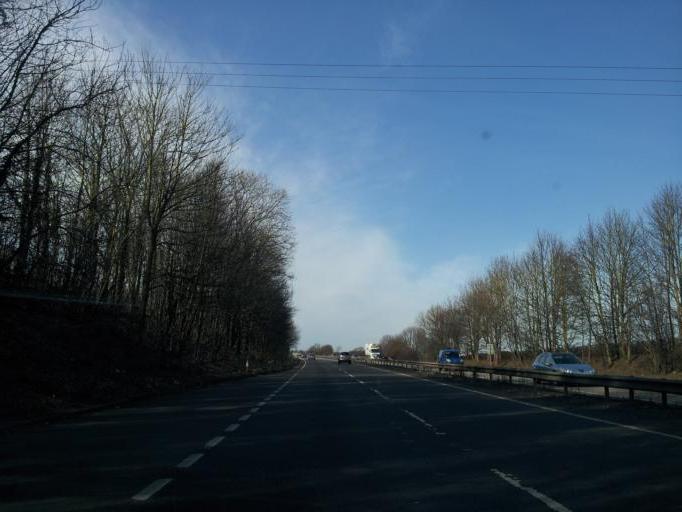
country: GB
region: England
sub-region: Lincolnshire
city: Grantham
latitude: 52.8800
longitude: -0.6354
